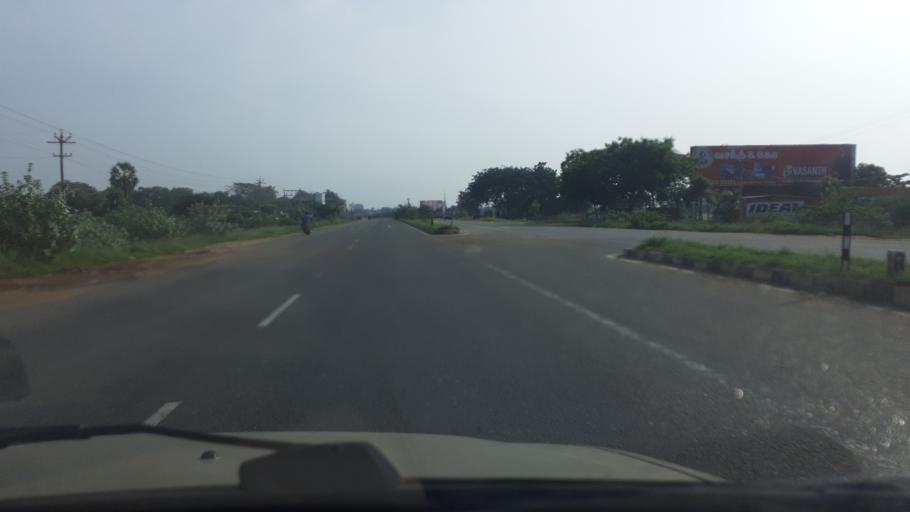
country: IN
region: Tamil Nadu
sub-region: Tirunelveli Kattabo
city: Nanguneri
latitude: 8.6074
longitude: 77.6841
